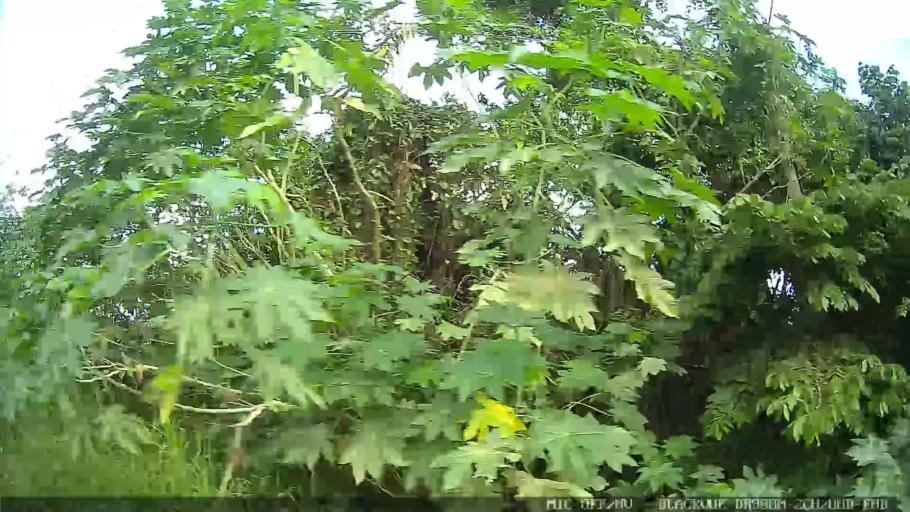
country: BR
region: Sao Paulo
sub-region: Itanhaem
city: Itanhaem
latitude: -24.1946
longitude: -46.8264
